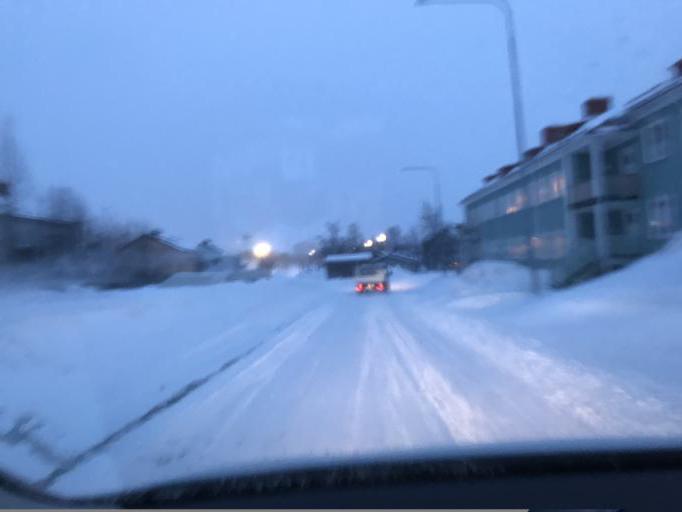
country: SE
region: Norrbotten
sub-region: Kiruna Kommun
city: Kiruna
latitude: 67.8652
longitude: 20.2277
